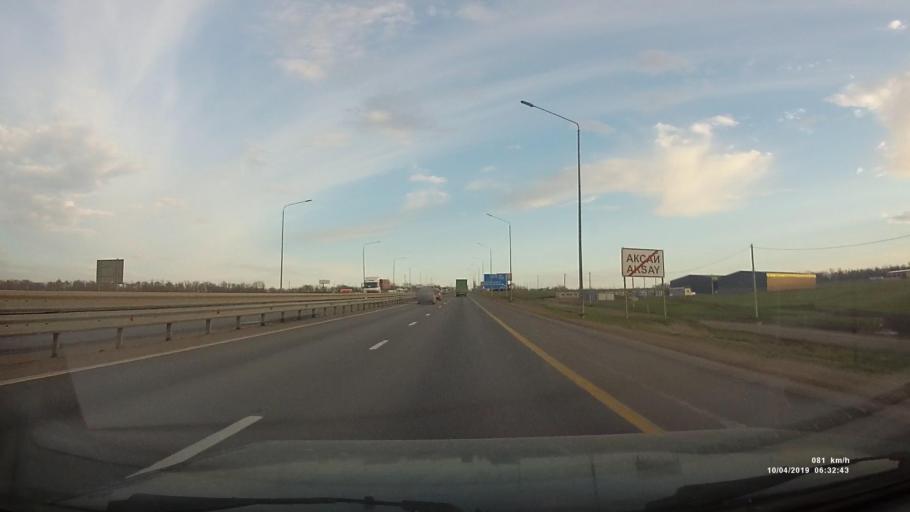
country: RU
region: Rostov
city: Aksay
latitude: 47.2787
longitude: 39.8519
